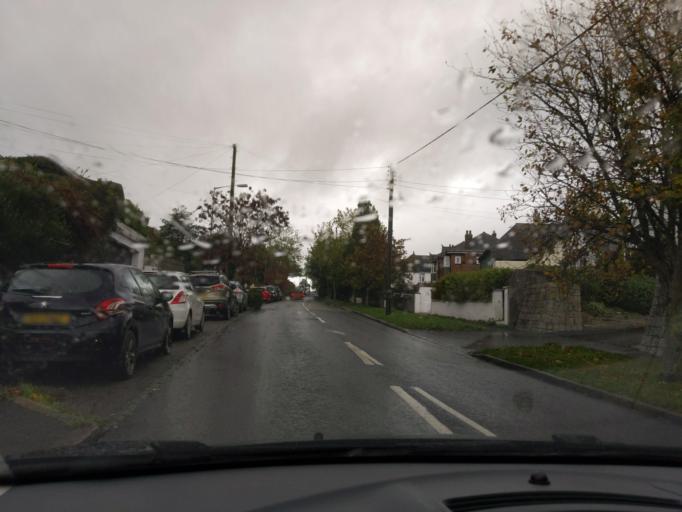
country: GB
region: England
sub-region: Cornwall
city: Wadebridge
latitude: 50.5171
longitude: -4.8424
